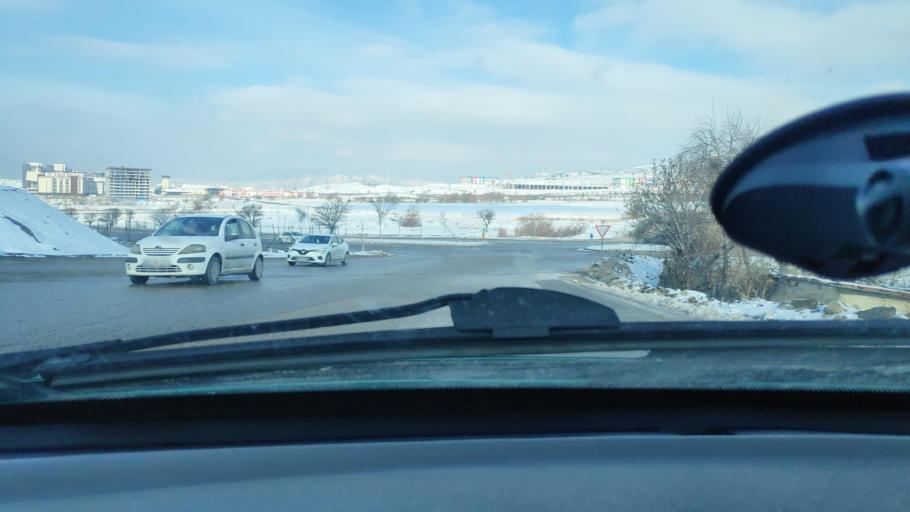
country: TR
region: Ankara
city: Ankara
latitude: 40.0149
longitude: 32.8363
